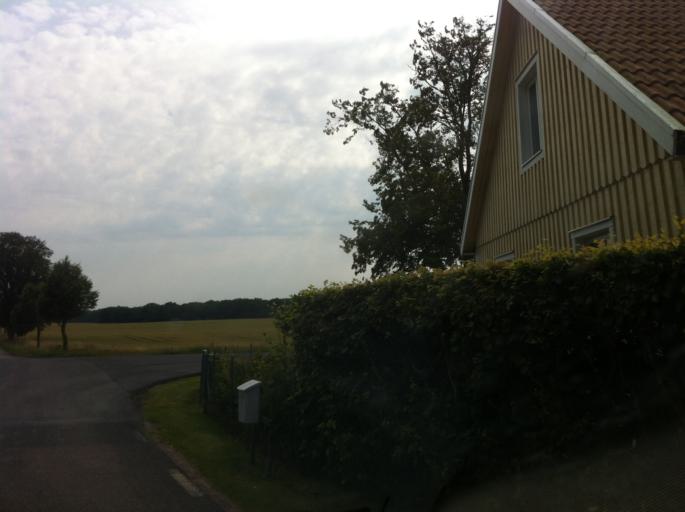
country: SE
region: Skane
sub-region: Eslovs Kommun
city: Eslov
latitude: 55.9184
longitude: 13.2463
